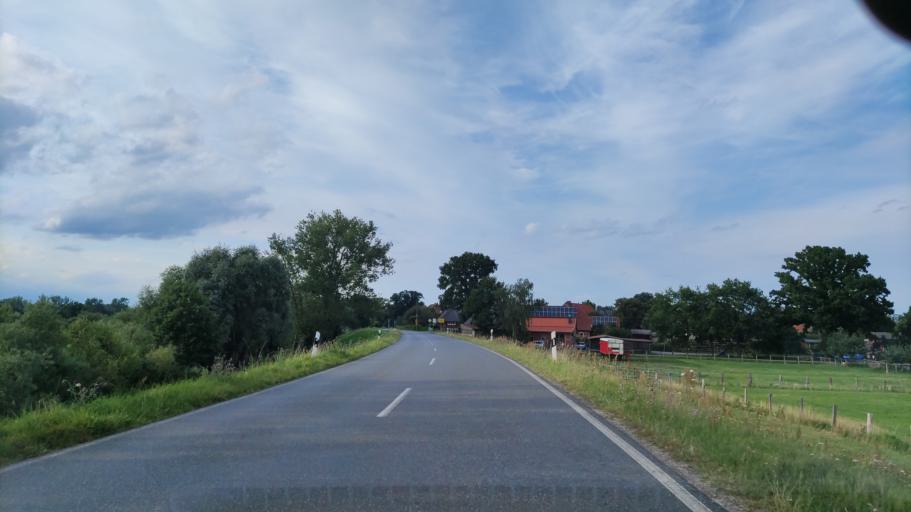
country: DE
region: Lower Saxony
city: Dannenberg
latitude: 53.1344
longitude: 11.1220
